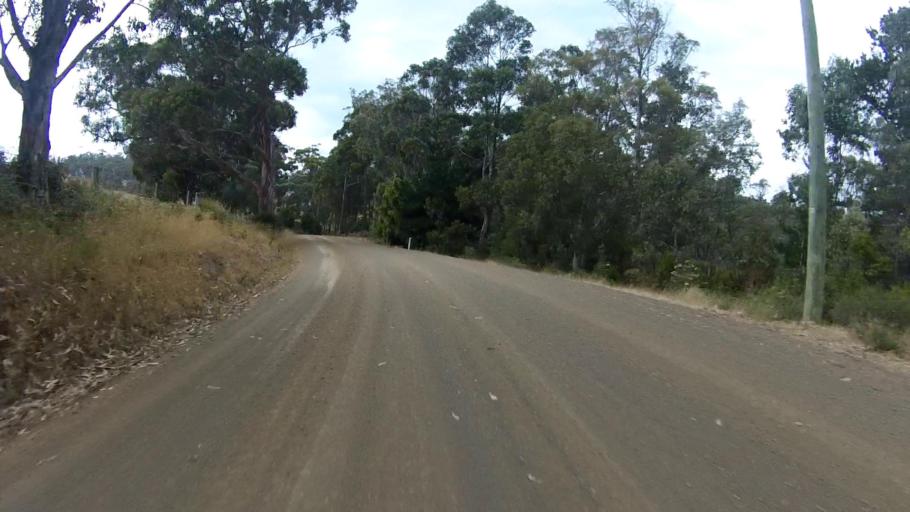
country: AU
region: Tasmania
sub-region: Huon Valley
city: Cygnet
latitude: -43.2365
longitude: 147.0989
